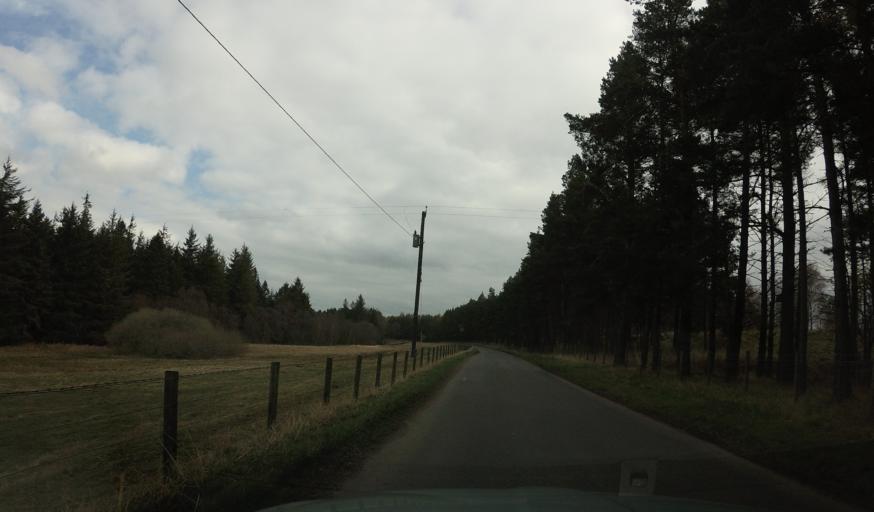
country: GB
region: Scotland
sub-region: Midlothian
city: Penicuik
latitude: 55.7683
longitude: -3.1383
